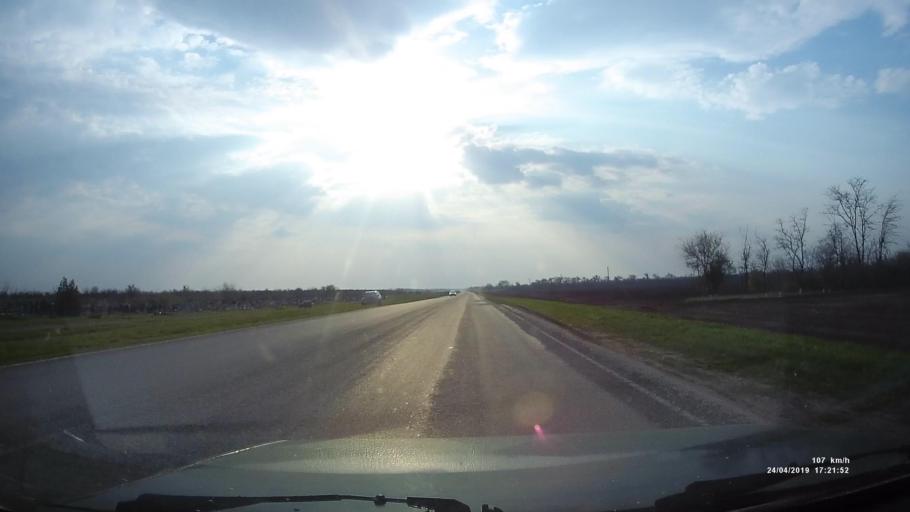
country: RU
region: Rostov
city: Gigant
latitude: 46.5203
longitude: 41.3229
